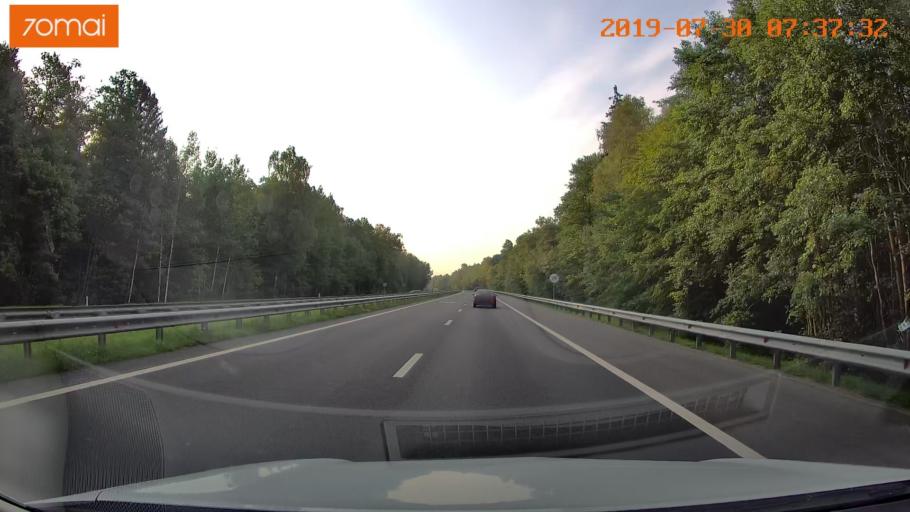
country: RU
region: Kaliningrad
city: Gvardeysk
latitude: 54.6552
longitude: 21.1477
